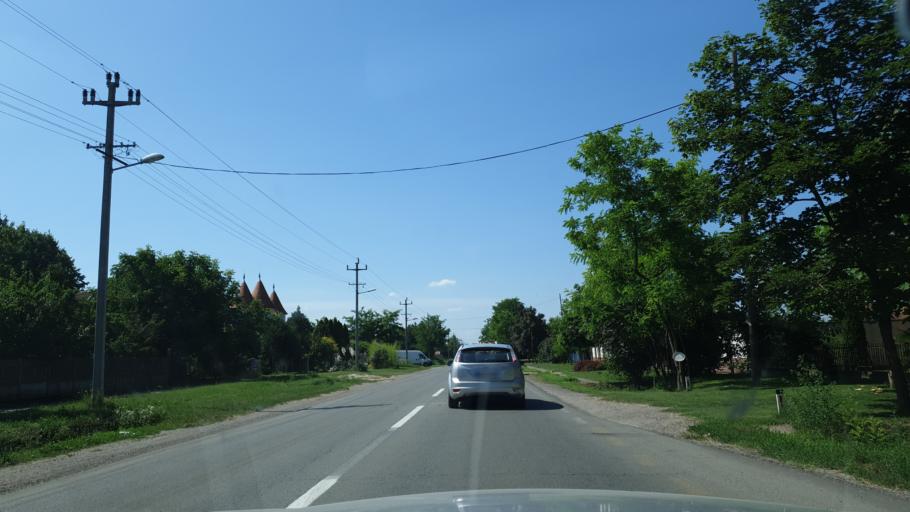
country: HU
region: Bacs-Kiskun
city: Kelebia
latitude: 46.1432
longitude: 19.5879
